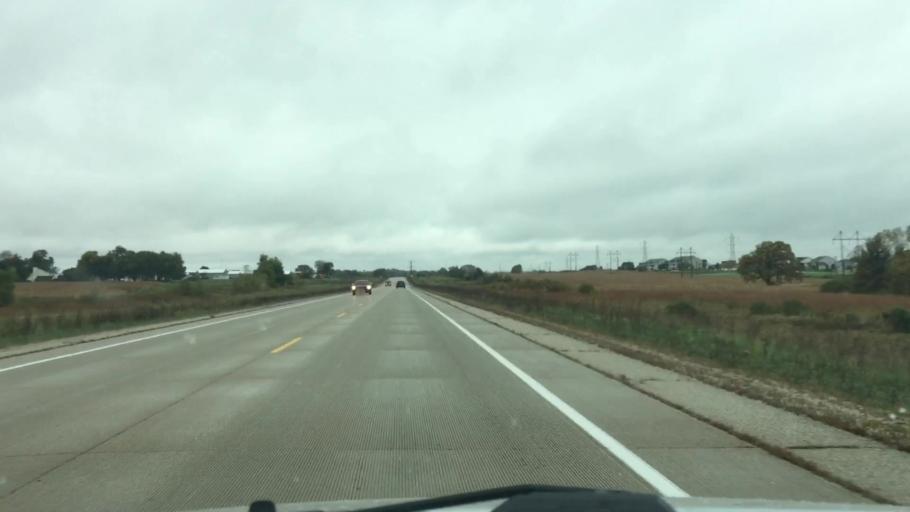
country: US
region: Wisconsin
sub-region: Walworth County
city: Whitewater
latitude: 42.8192
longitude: -88.7148
